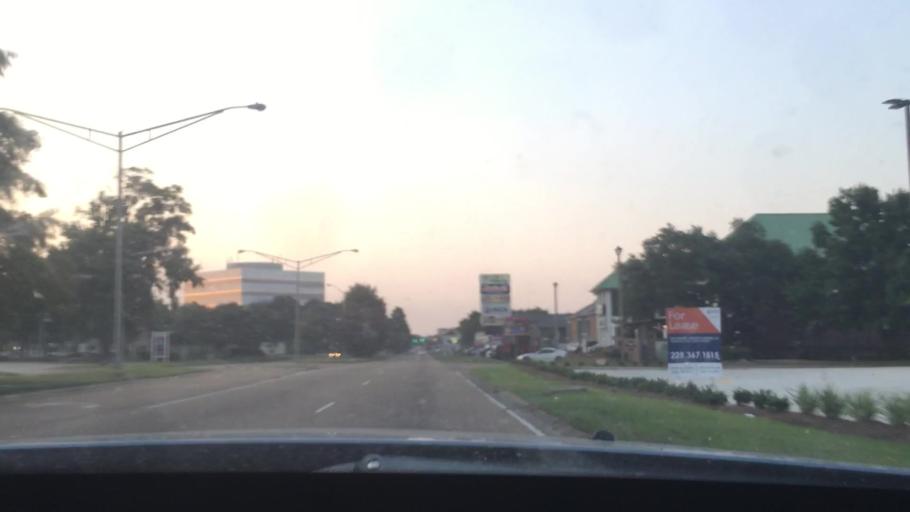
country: US
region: Louisiana
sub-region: East Baton Rouge Parish
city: Inniswold
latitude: 30.4141
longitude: -91.0516
